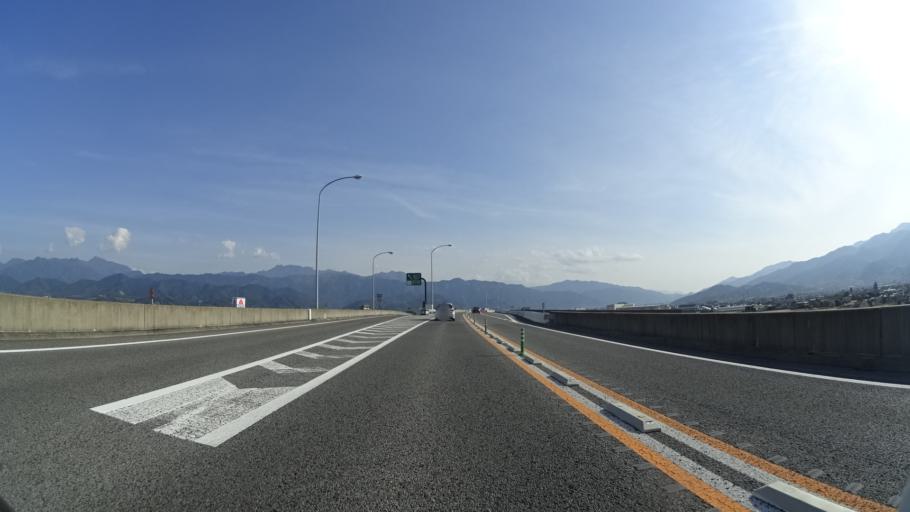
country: JP
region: Ehime
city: Saijo
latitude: 33.9210
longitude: 133.0744
